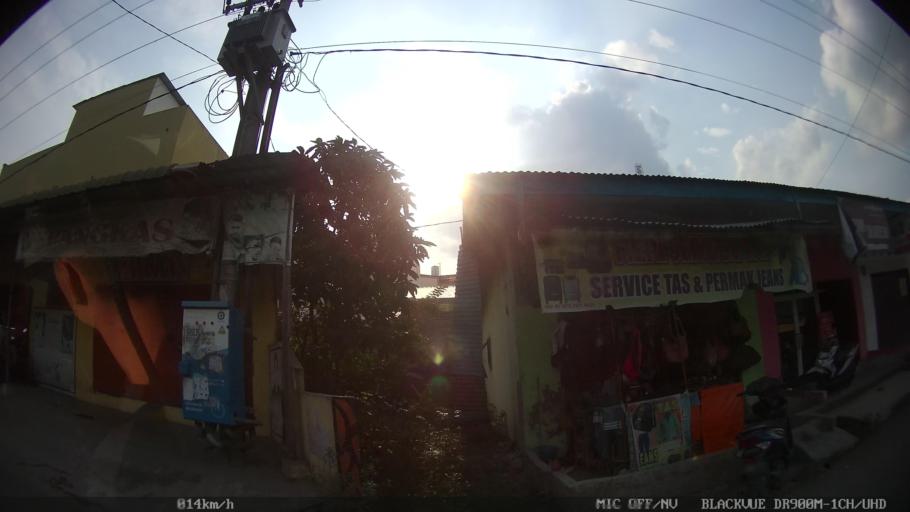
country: ID
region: North Sumatra
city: Medan
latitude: 3.5864
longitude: 98.7408
